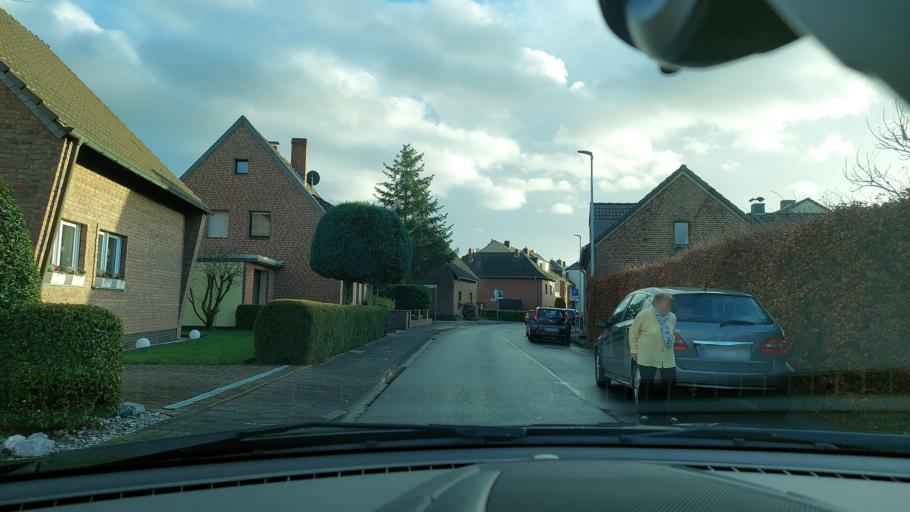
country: DE
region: North Rhine-Westphalia
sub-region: Regierungsbezirk Koln
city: Sinnersdorf
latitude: 51.0571
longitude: 6.8170
